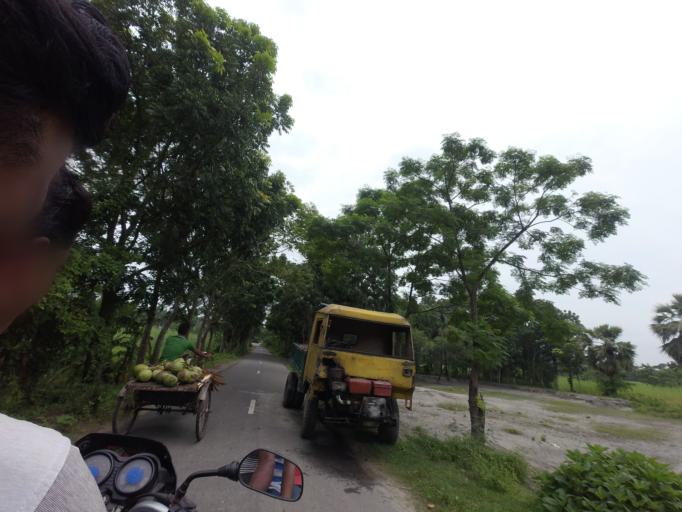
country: BD
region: Khulna
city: Kalia
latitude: 23.1097
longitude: 89.6470
